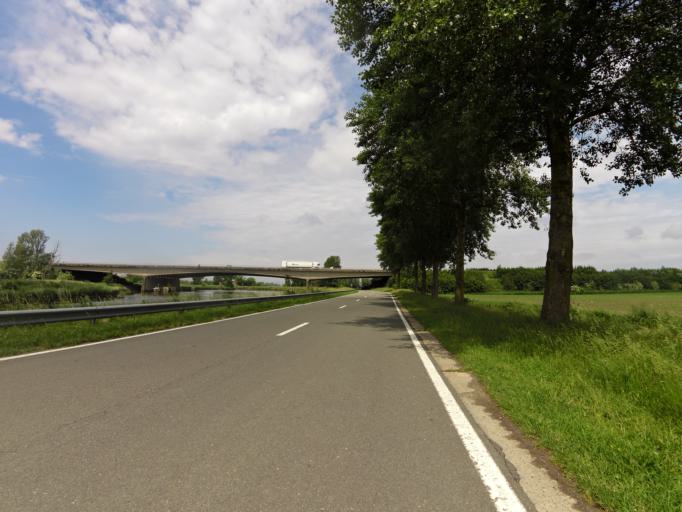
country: BE
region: Flanders
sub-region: Provincie West-Vlaanderen
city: Nieuwpoort
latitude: 51.1278
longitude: 2.8019
